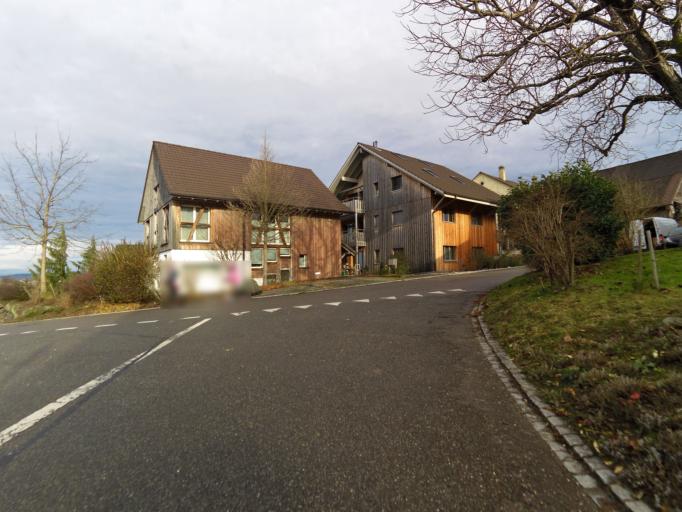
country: CH
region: Thurgau
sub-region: Frauenfeld District
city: Frauenfeld
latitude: 47.5492
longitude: 8.9215
